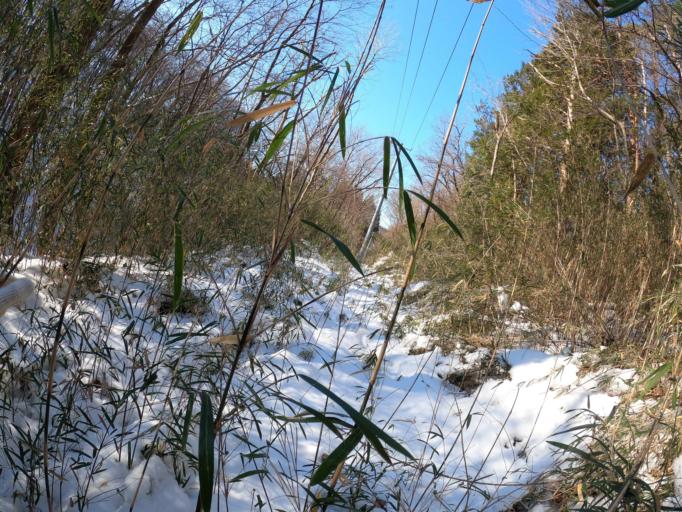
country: JP
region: Iwate
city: Ichinoseki
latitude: 38.9041
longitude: 141.1221
